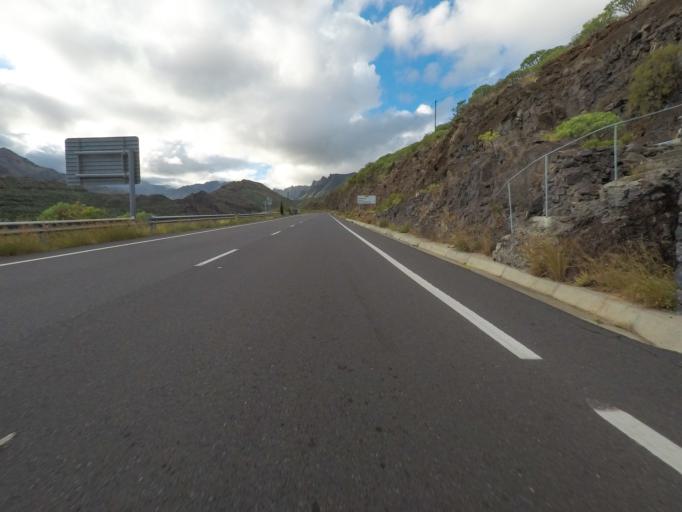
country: ES
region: Canary Islands
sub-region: Provincia de Santa Cruz de Tenerife
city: San Sebastian de la Gomera
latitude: 28.1115
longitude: -17.1314
